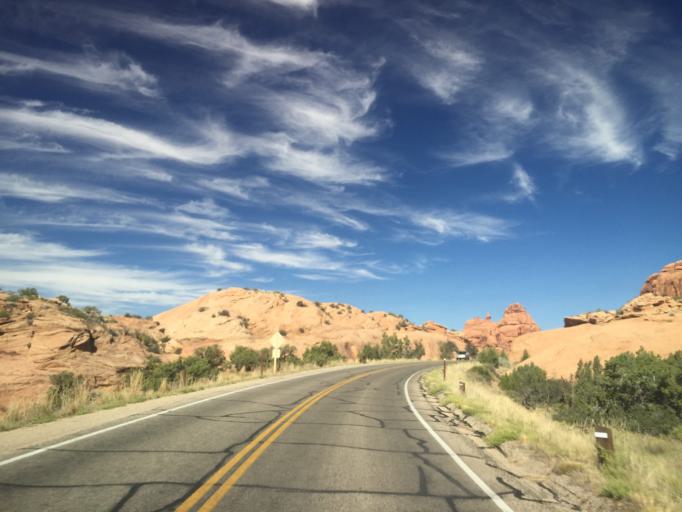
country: US
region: Utah
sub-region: Grand County
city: Moab
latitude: 38.6912
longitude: -109.5441
